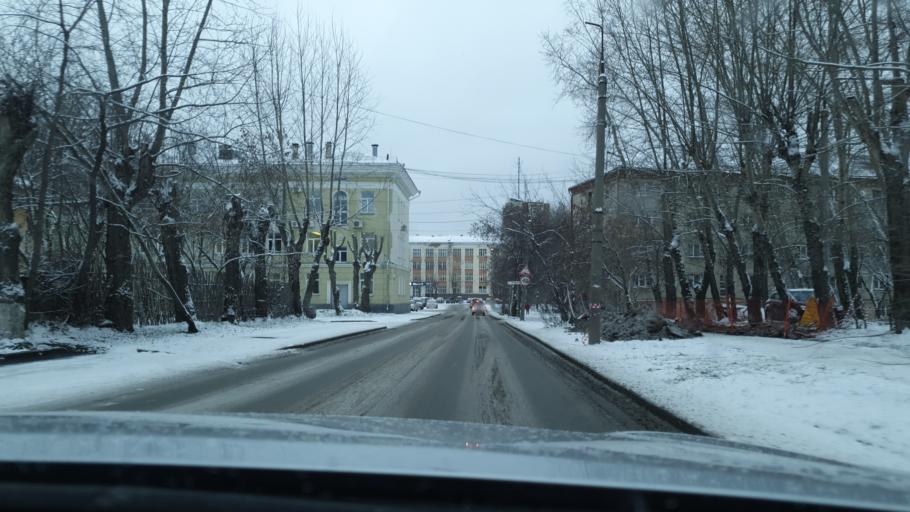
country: RU
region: Sverdlovsk
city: Istok
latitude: 56.7579
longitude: 60.7104
